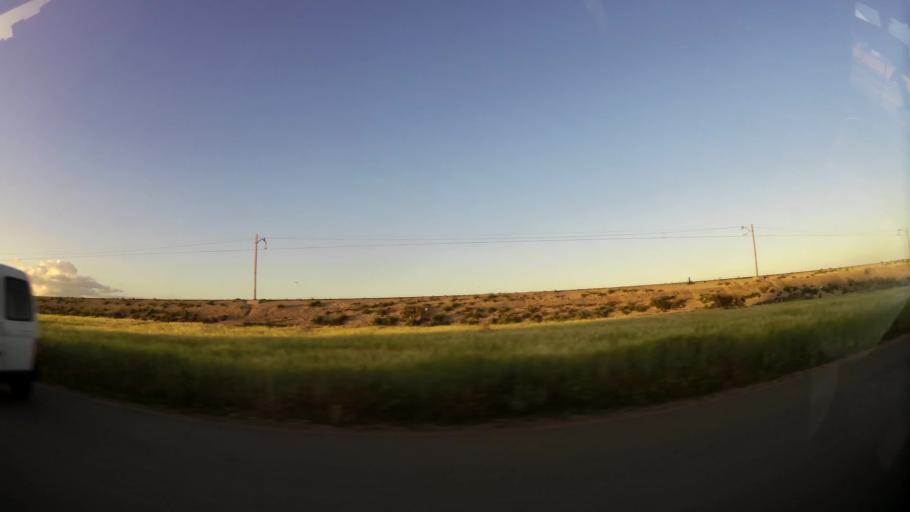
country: MA
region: Marrakech-Tensift-Al Haouz
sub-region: Kelaa-Des-Sraghna
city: Sidi Abdallah
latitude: 32.2399
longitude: -7.9304
